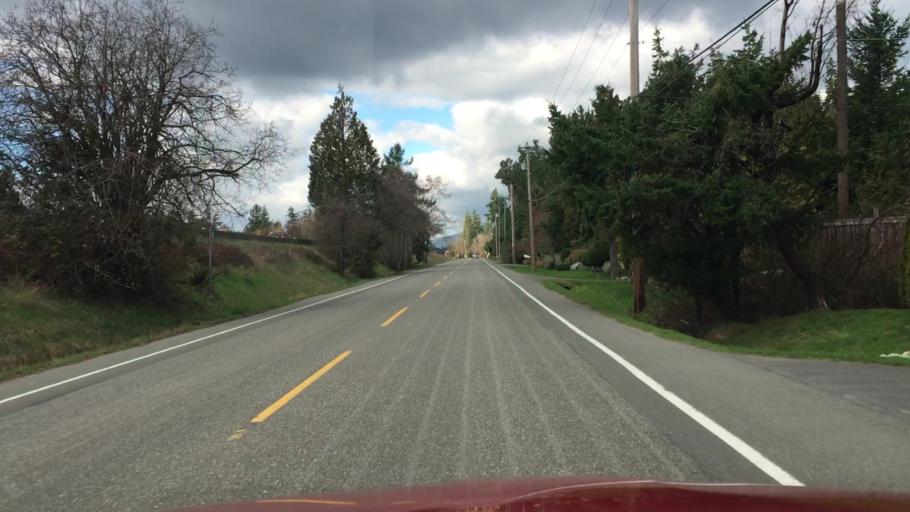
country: CA
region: British Columbia
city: North Saanich
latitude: 48.6082
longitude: -123.3976
